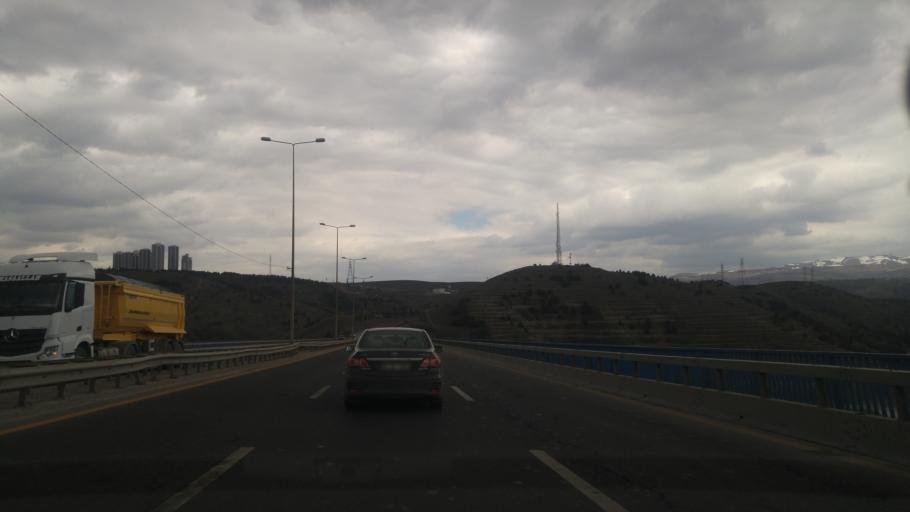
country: TR
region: Ankara
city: Mamak
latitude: 39.8894
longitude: 32.9062
